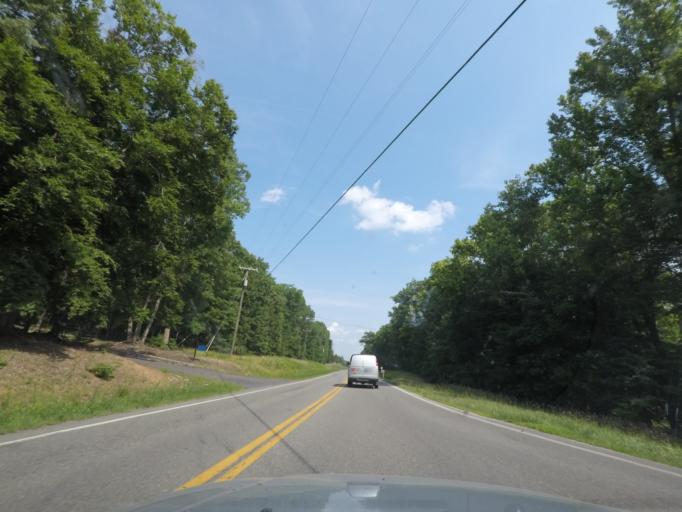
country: US
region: Virginia
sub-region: Fluvanna County
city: Palmyra
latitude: 37.8207
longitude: -78.2667
